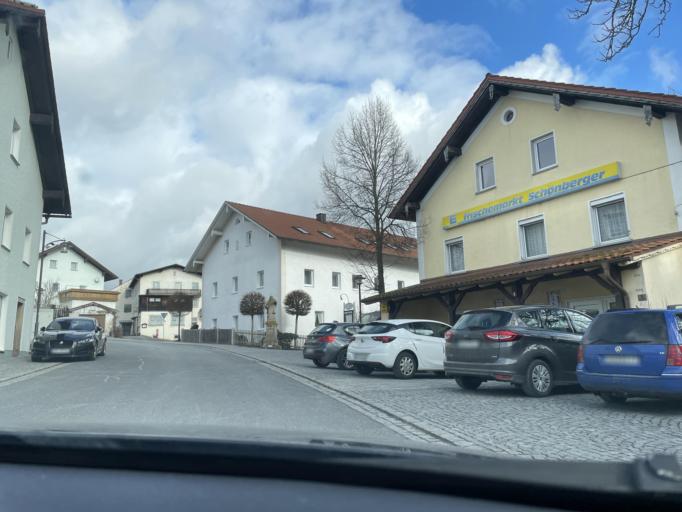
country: DE
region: Bavaria
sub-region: Upper Palatinate
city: Runding
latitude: 49.2148
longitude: 12.7641
